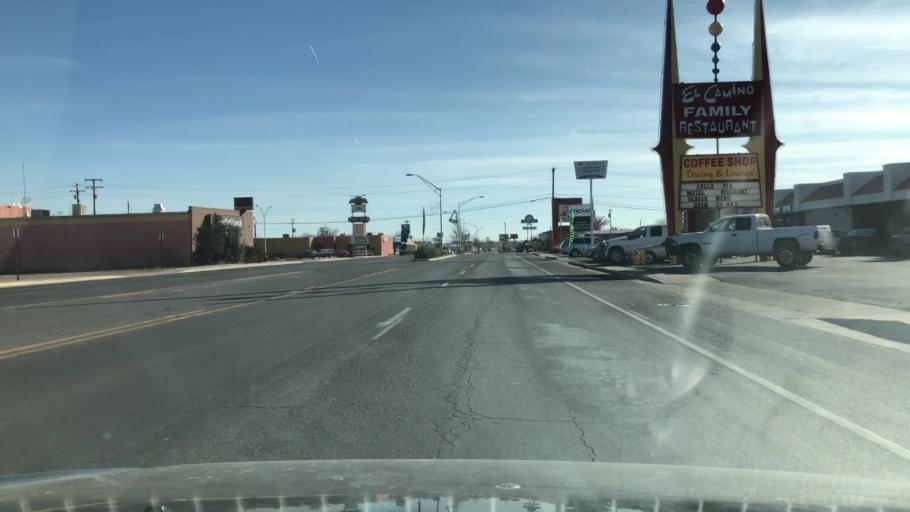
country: US
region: New Mexico
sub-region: Socorro County
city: Socorro
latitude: 34.0646
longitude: -106.8926
